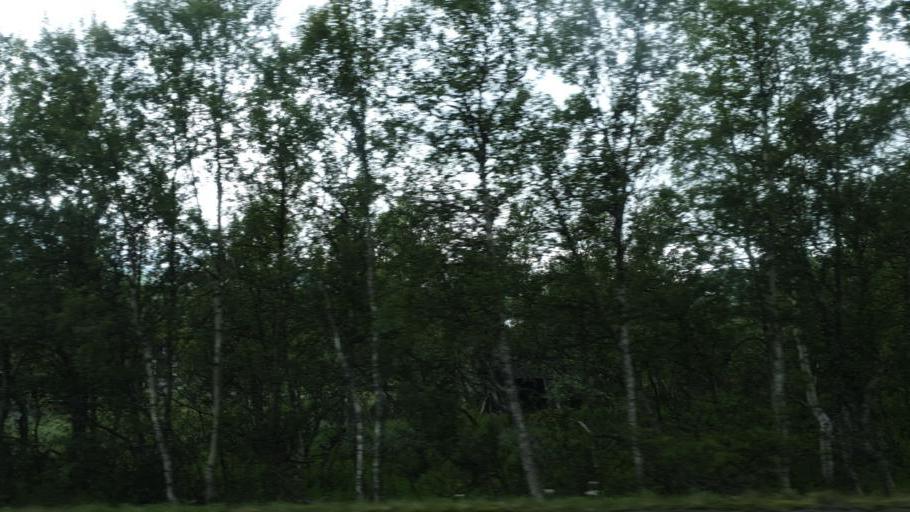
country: NO
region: Oppland
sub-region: Vestre Slidre
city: Slidre
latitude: 61.2584
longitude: 8.8748
